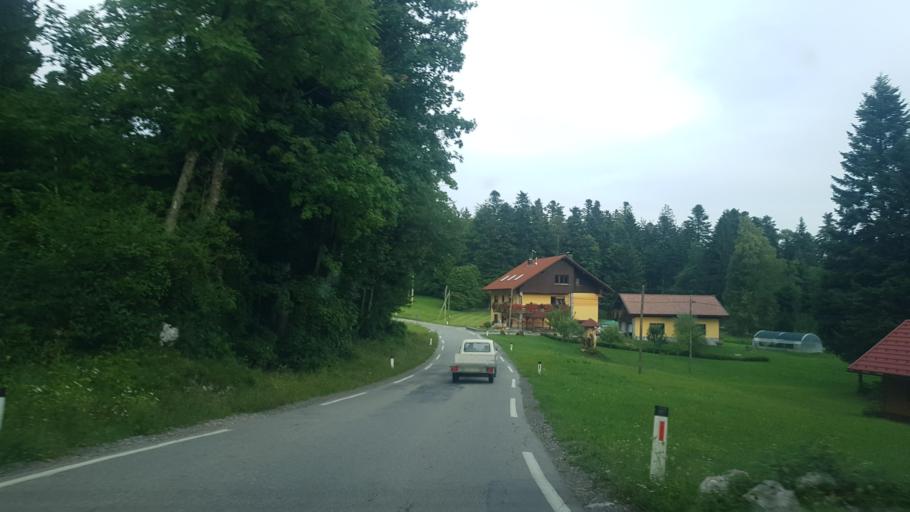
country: SI
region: Vipava
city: Vipava
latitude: 45.8617
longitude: 14.0908
